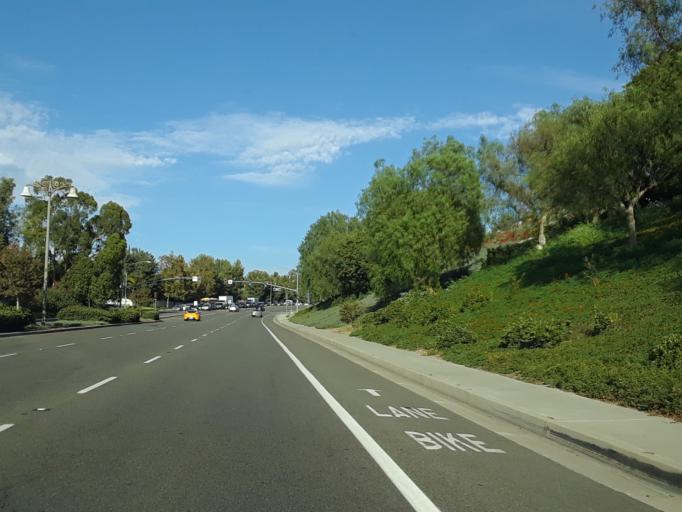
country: US
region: California
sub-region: Orange County
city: Ladera Ranch
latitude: 33.5869
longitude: -117.6496
